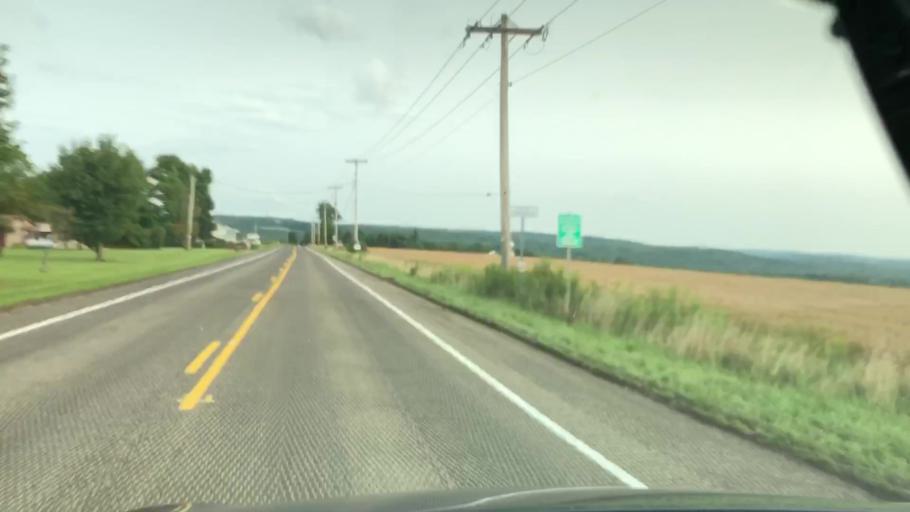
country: US
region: Pennsylvania
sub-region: Crawford County
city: Titusville
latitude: 41.7490
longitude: -79.7699
